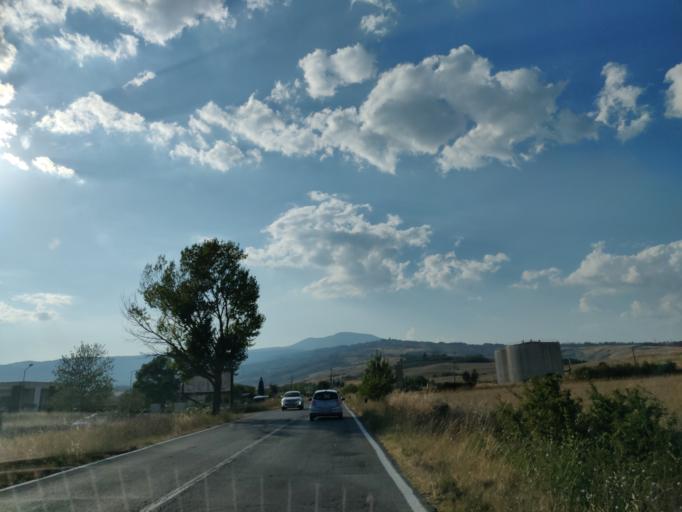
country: IT
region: Tuscany
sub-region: Provincia di Siena
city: Piancastagnaio
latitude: 42.8238
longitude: 11.7272
